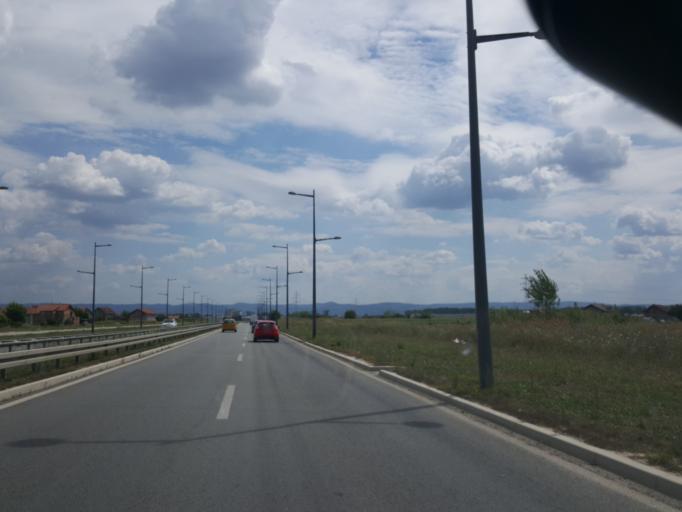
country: RS
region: Autonomna Pokrajina Vojvodina
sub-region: Juznobacki Okrug
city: Novi Sad
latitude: 45.2991
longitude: 19.8077
